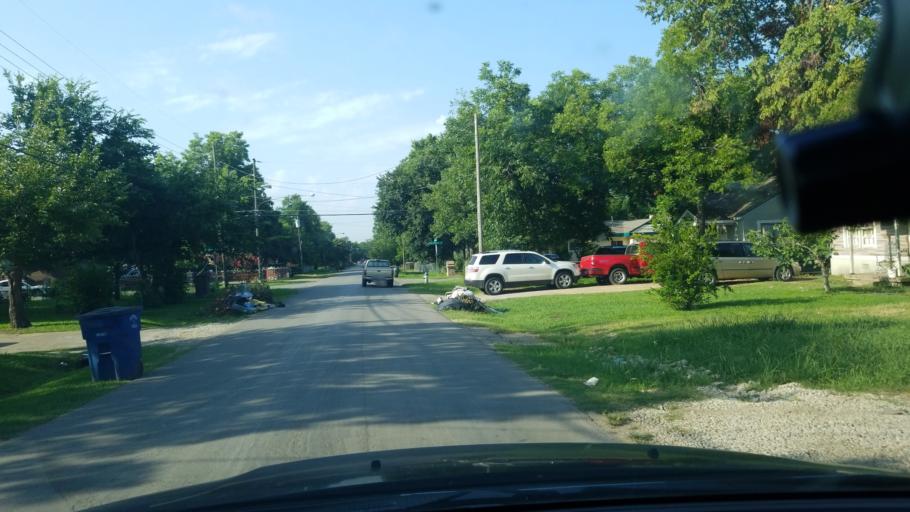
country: US
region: Texas
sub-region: Dallas County
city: Balch Springs
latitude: 32.7294
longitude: -96.6865
